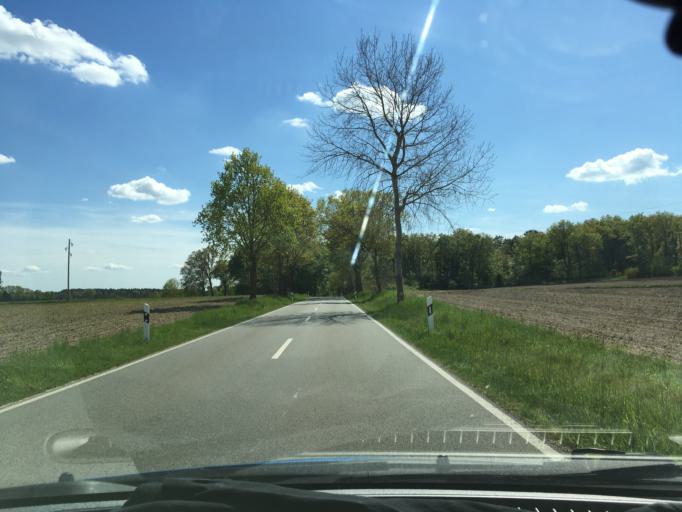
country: DE
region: Lower Saxony
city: Zernien
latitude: 53.0300
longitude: 10.8870
